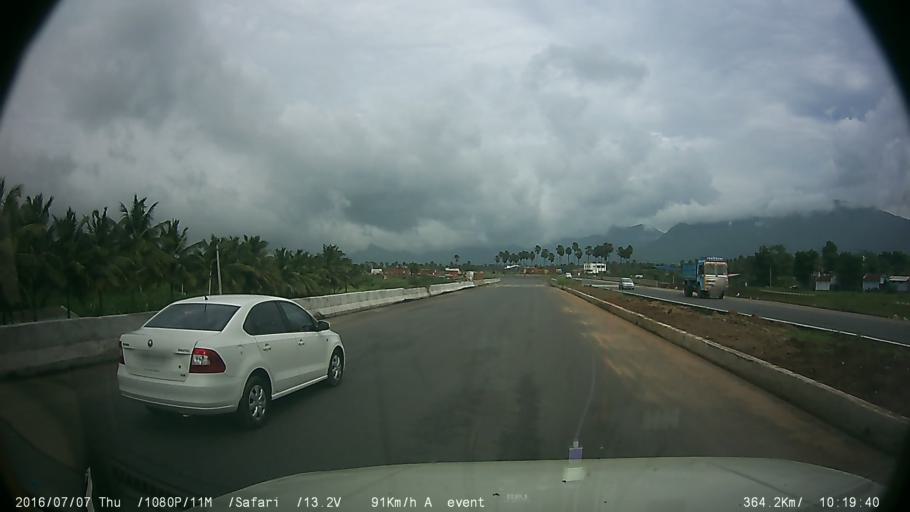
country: IN
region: Tamil Nadu
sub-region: Coimbatore
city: Madukkarai
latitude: 10.8719
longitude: 76.8934
